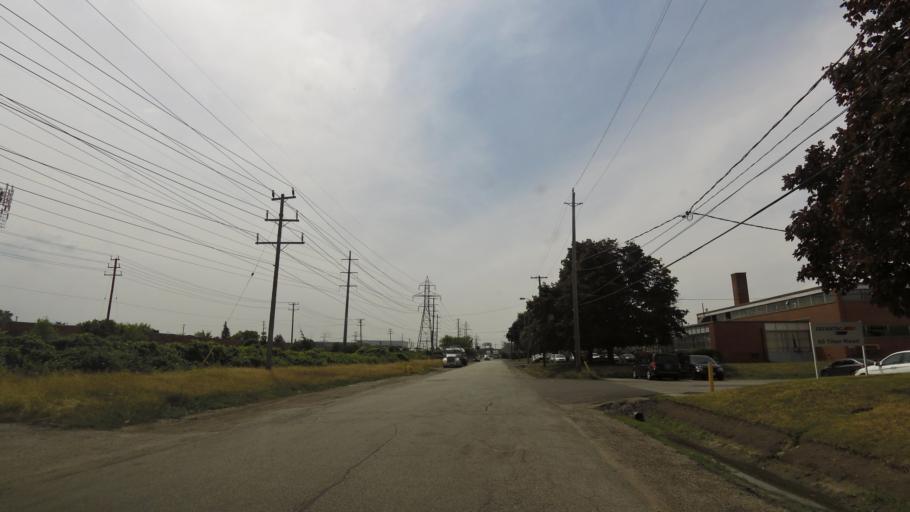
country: CA
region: Ontario
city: Etobicoke
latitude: 43.6297
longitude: -79.5233
